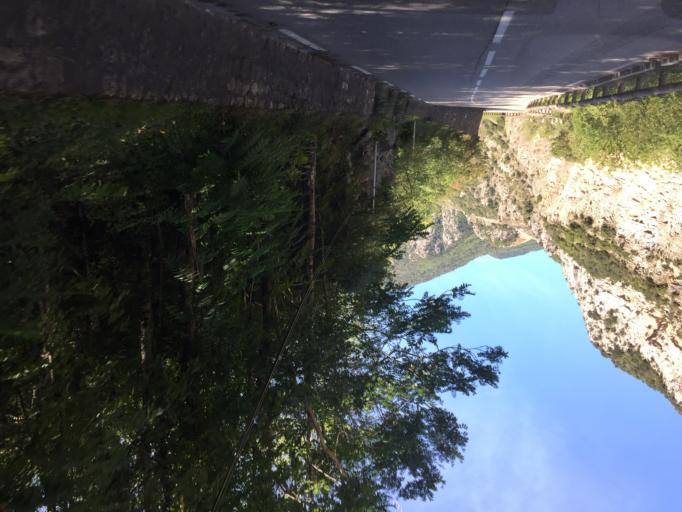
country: FR
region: Provence-Alpes-Cote d'Azur
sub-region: Departement des Alpes-Maritimes
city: Gilette
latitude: 43.9316
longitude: 7.1760
